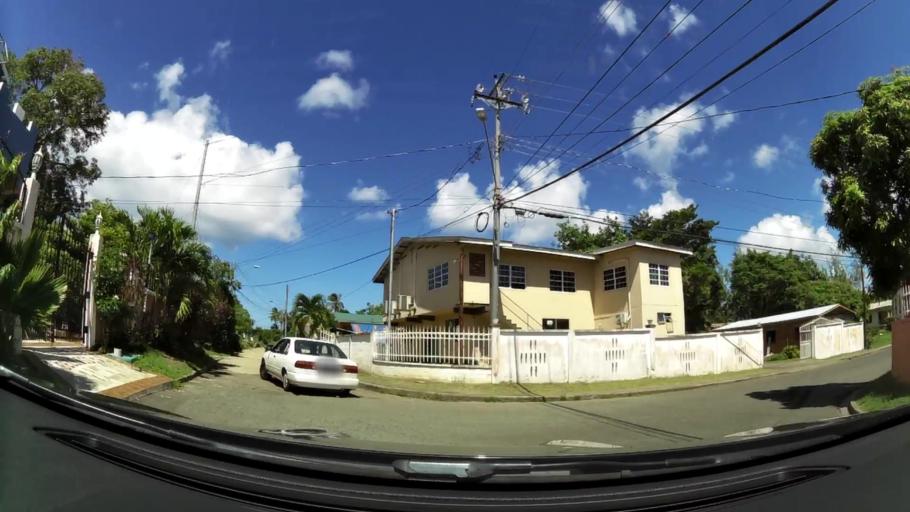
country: TT
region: Tobago
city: Scarborough
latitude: 11.1830
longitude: -60.8038
